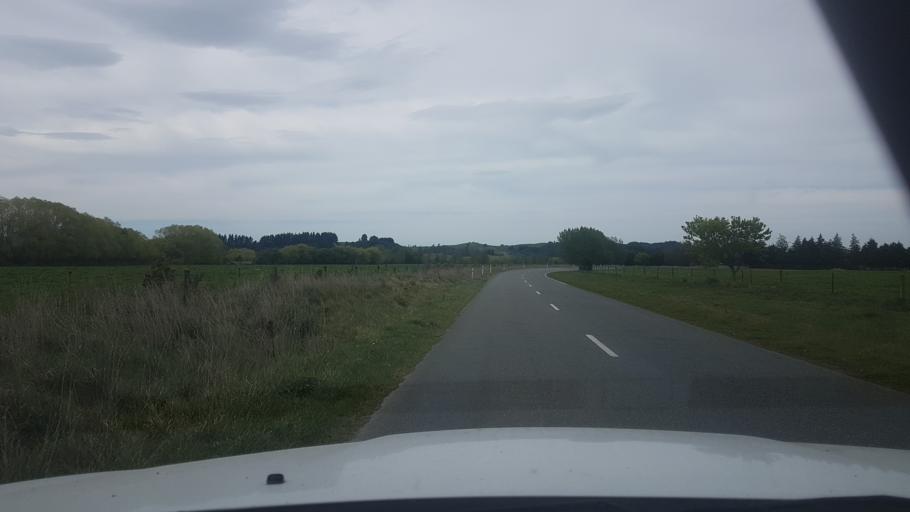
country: NZ
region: Canterbury
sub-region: Timaru District
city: Pleasant Point
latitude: -44.0726
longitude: 171.1633
